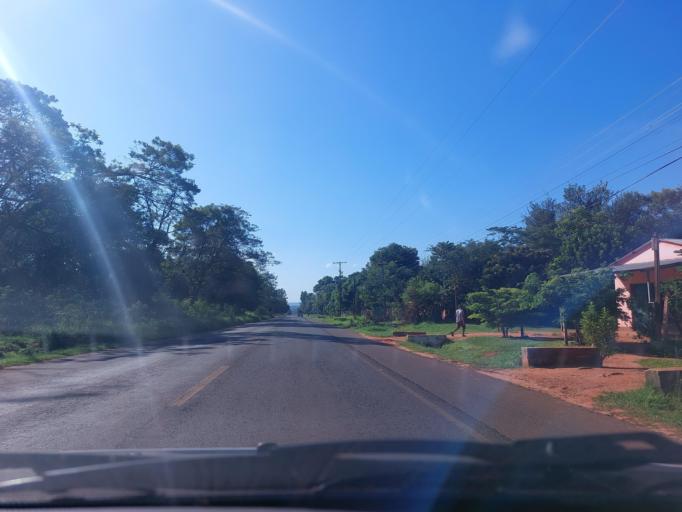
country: PY
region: San Pedro
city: Guayaybi
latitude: -24.5314
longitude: -56.4358
